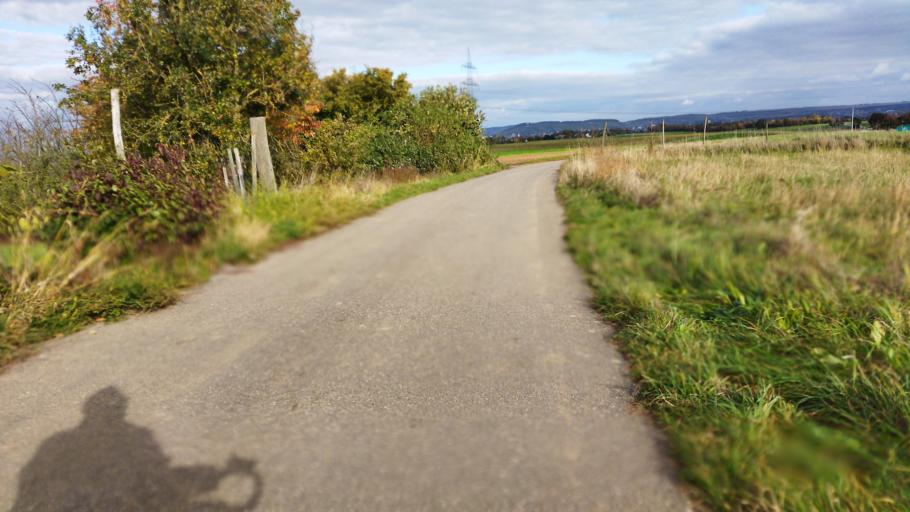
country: DE
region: Baden-Wuerttemberg
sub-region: Regierungsbezirk Stuttgart
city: Nordheim
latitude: 49.1257
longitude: 9.1398
